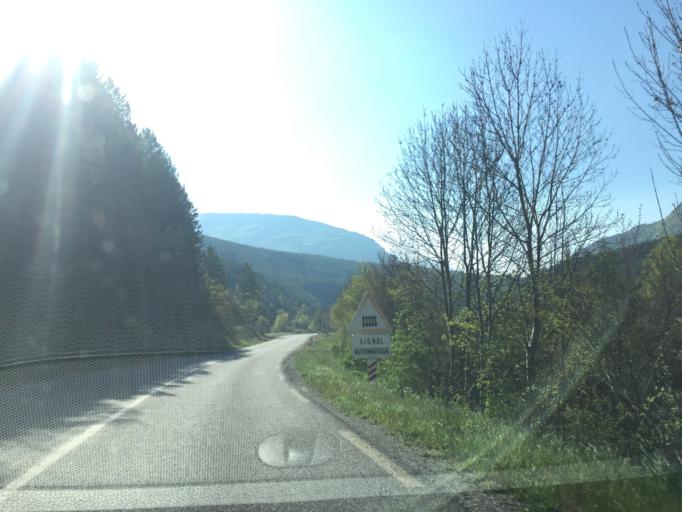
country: FR
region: Provence-Alpes-Cote d'Azur
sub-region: Departement des Hautes-Alpes
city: Veynes
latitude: 44.5652
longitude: 5.7580
